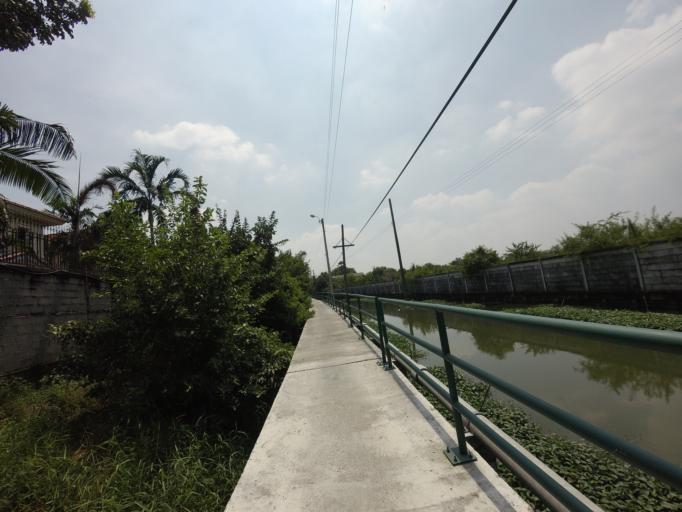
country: TH
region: Bangkok
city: Saphan Sung
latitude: 13.7655
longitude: 100.6690
